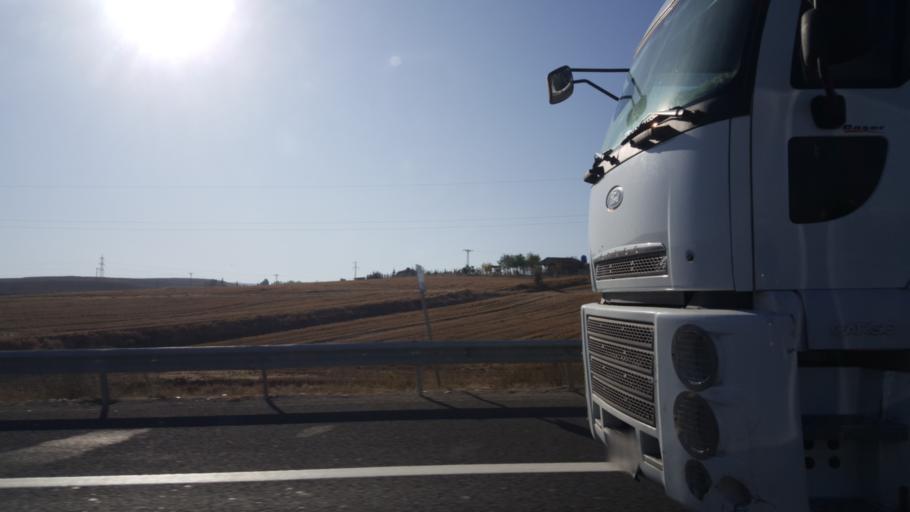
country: TR
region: Ankara
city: Mamak
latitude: 39.9028
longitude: 32.9931
